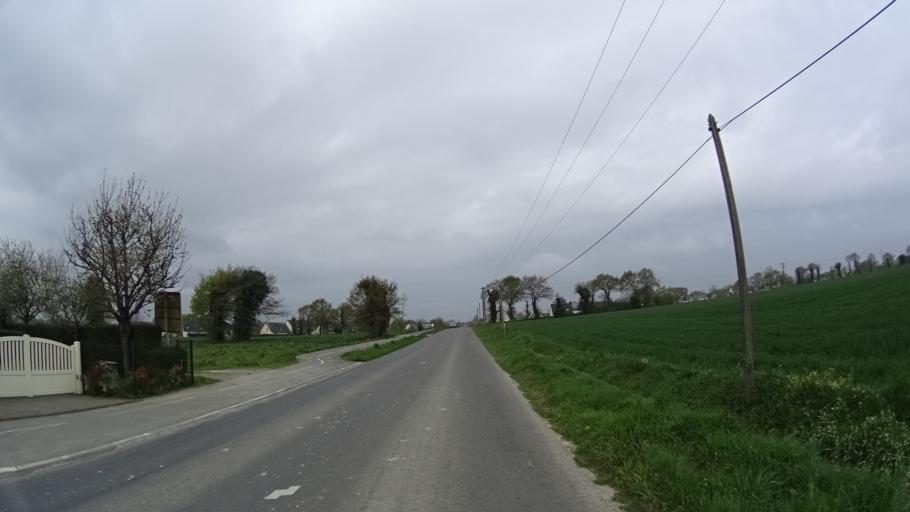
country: FR
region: Brittany
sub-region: Departement d'Ille-et-Vilaine
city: La Chapelle-Thouarault
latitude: 48.1230
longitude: -1.8567
